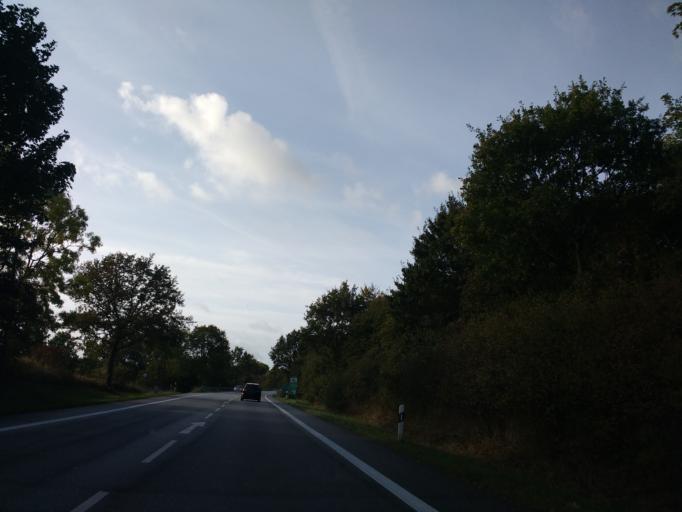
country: DE
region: Schleswig-Holstein
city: Schashagen
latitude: 54.1237
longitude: 10.8775
